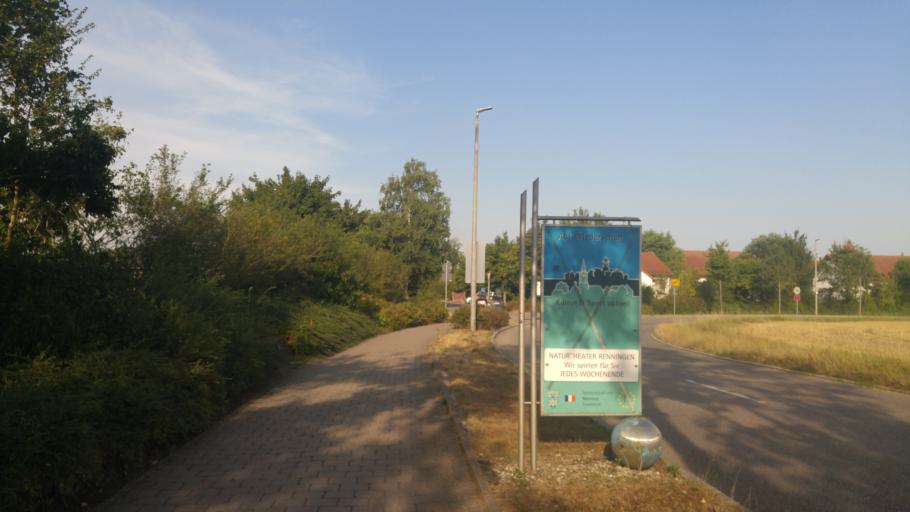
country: DE
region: Baden-Wuerttemberg
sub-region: Regierungsbezirk Stuttgart
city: Renningen
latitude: 48.7702
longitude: 8.9246
